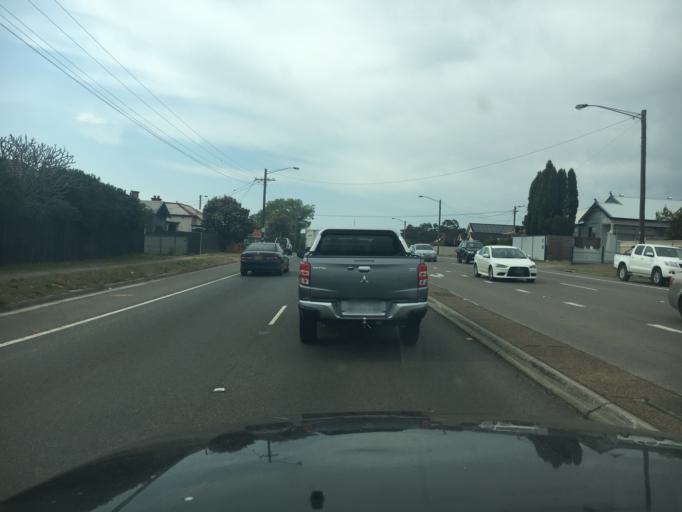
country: AU
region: New South Wales
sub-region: Maitland Municipality
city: East Maitland
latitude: -32.7547
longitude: 151.5884
